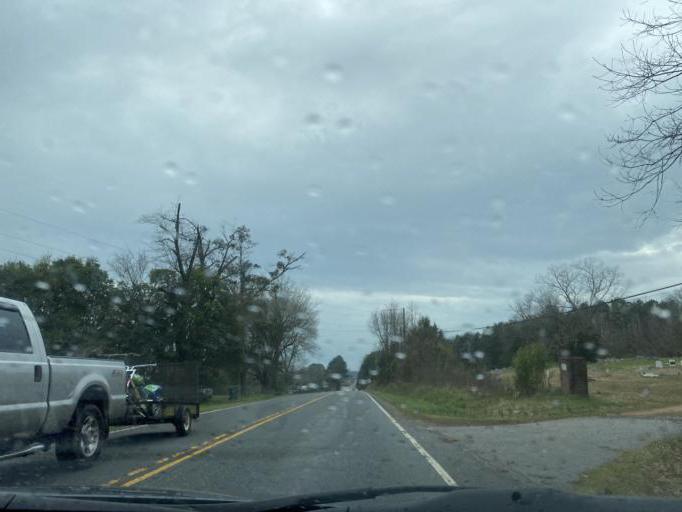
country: US
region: South Carolina
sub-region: Cherokee County
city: Gaffney
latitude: 35.0292
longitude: -81.7069
